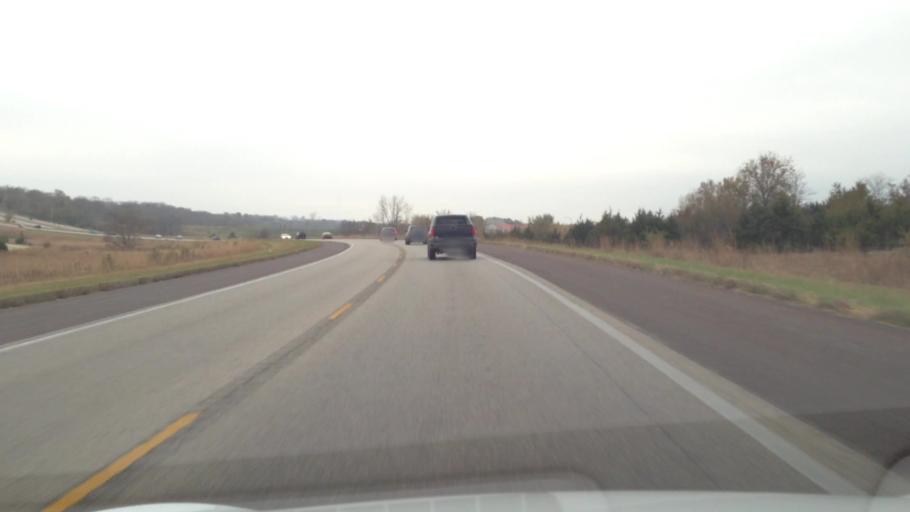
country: US
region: Kansas
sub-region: Douglas County
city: Lawrence
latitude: 38.9403
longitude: -95.3113
